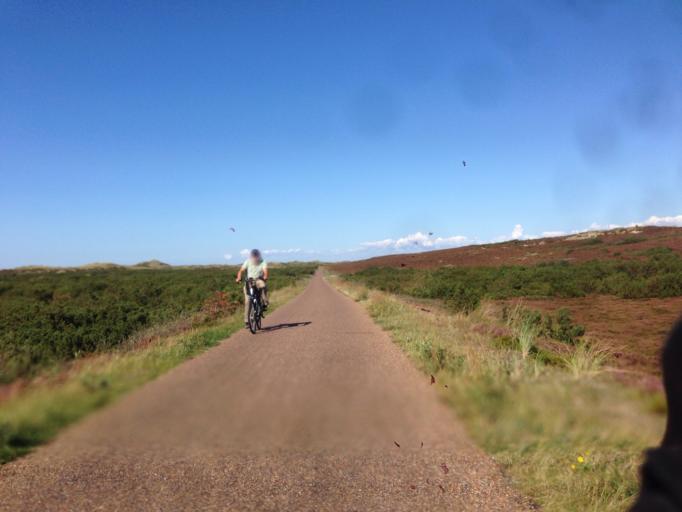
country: DE
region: Schleswig-Holstein
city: Tinnum
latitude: 54.9783
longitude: 8.3574
